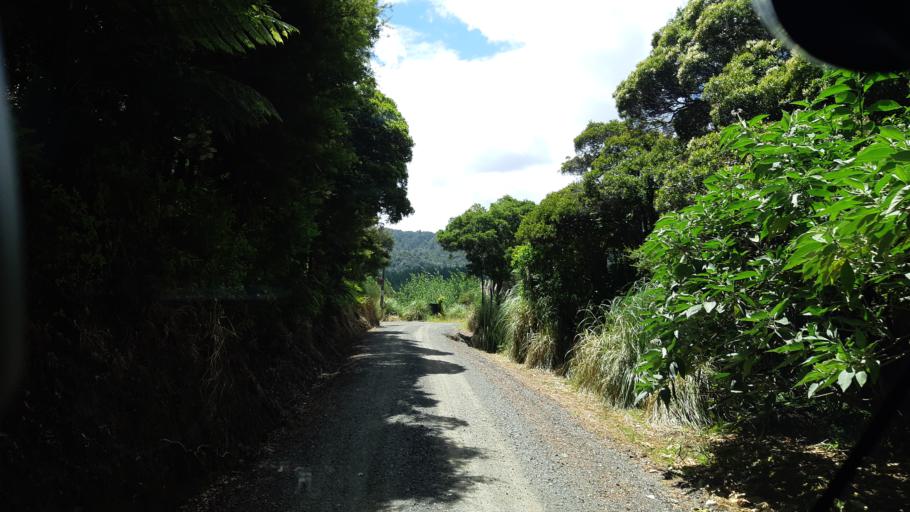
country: NZ
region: Northland
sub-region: Far North District
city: Kaitaia
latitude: -35.2281
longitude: 173.3106
